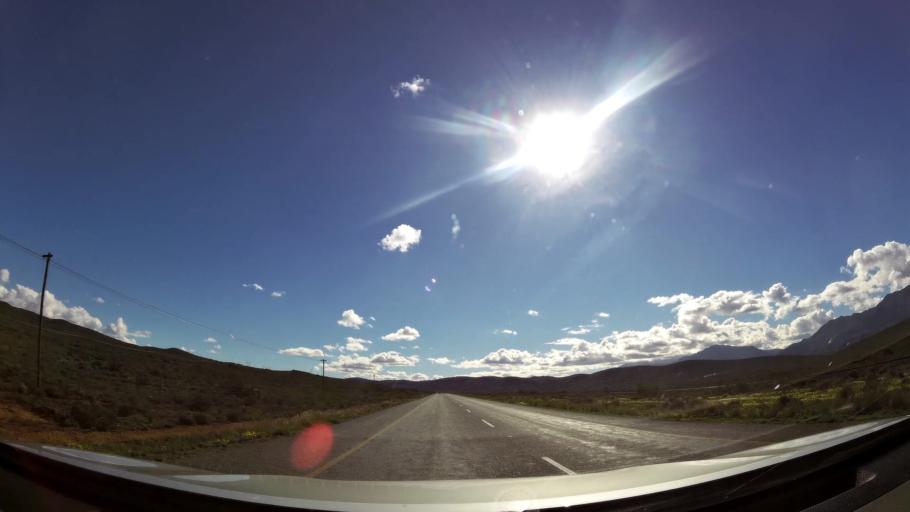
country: ZA
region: Western Cape
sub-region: Cape Winelands District Municipality
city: Worcester
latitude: -33.7475
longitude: 19.7036
